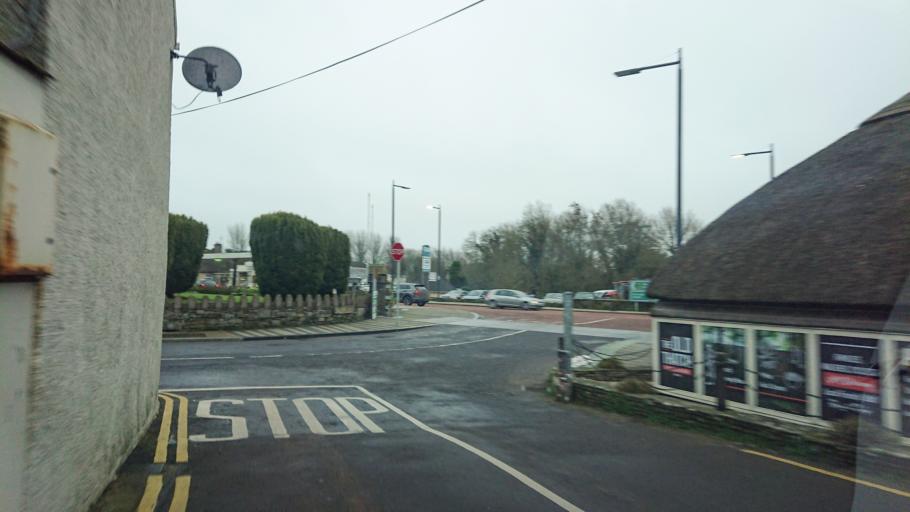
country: IE
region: Munster
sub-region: County Cork
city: Castlemartyr
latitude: 51.9428
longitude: -7.9924
